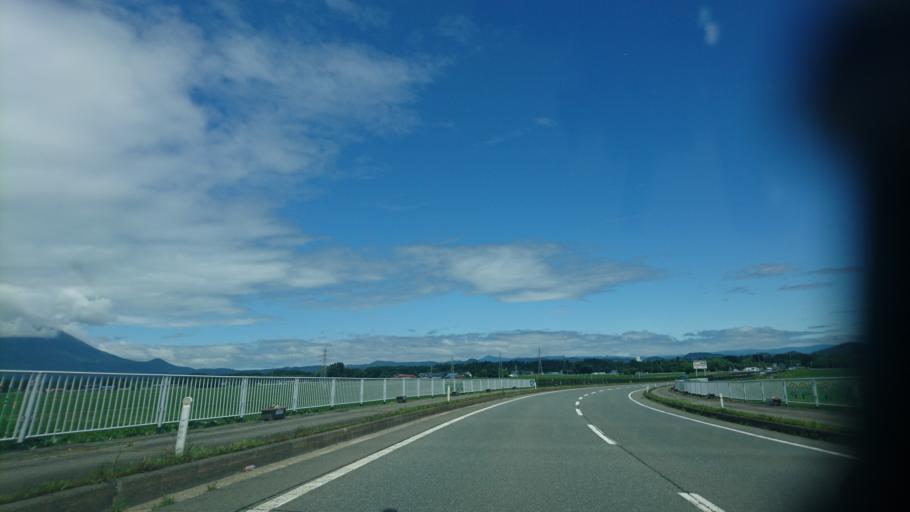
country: JP
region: Iwate
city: Shizukuishi
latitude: 39.6971
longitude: 140.9380
